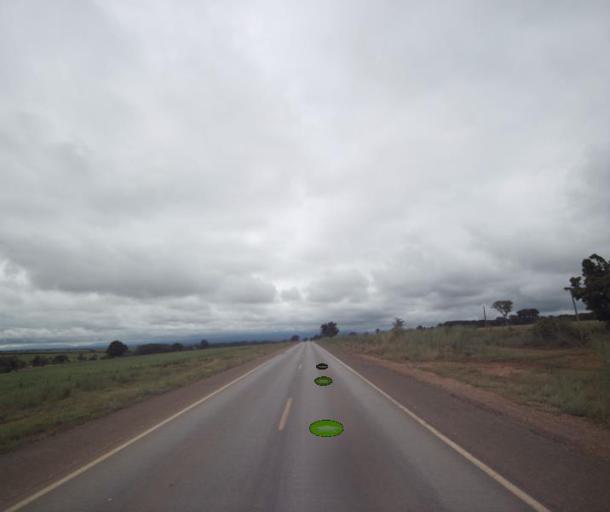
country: BR
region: Goias
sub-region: Uruacu
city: Uruacu
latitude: -14.6982
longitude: -49.1115
